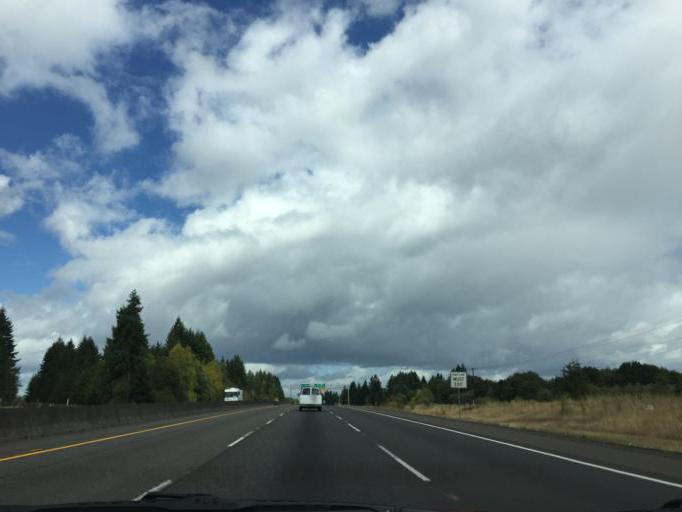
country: US
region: Washington
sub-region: Lewis County
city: Winlock
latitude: 46.4337
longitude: -122.8893
